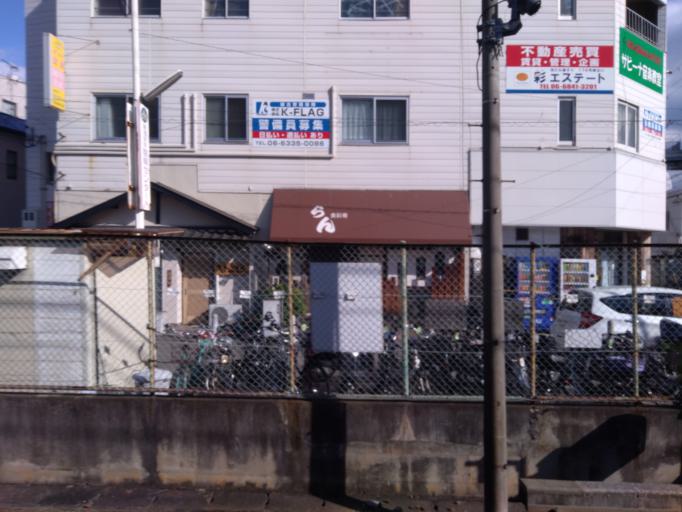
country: JP
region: Osaka
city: Toyonaka
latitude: 34.7954
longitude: 135.4489
